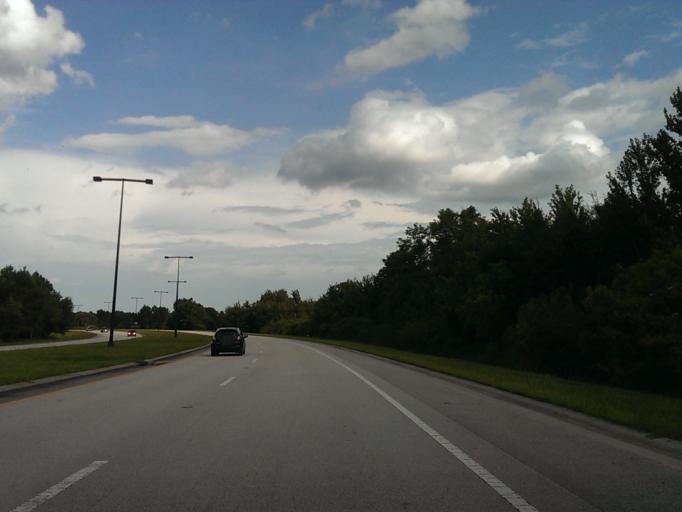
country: US
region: Florida
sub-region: Polk County
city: Citrus Ridge
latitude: 28.3737
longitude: -81.5977
